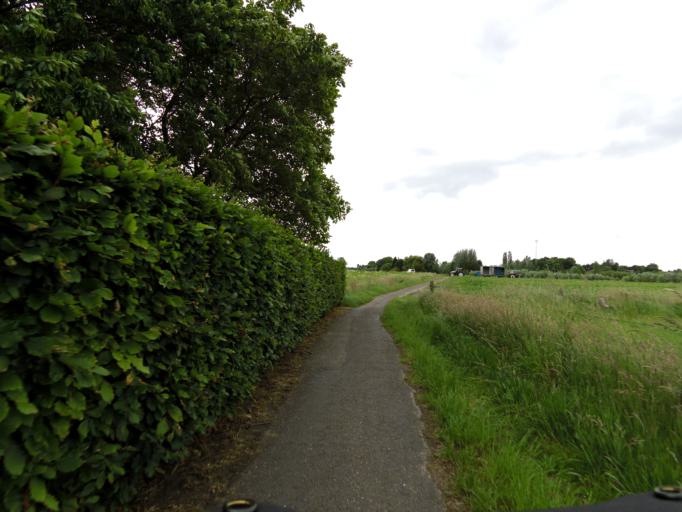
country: NL
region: North Brabant
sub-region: Gemeente Zundert
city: Zundert
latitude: 51.5202
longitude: 4.7123
